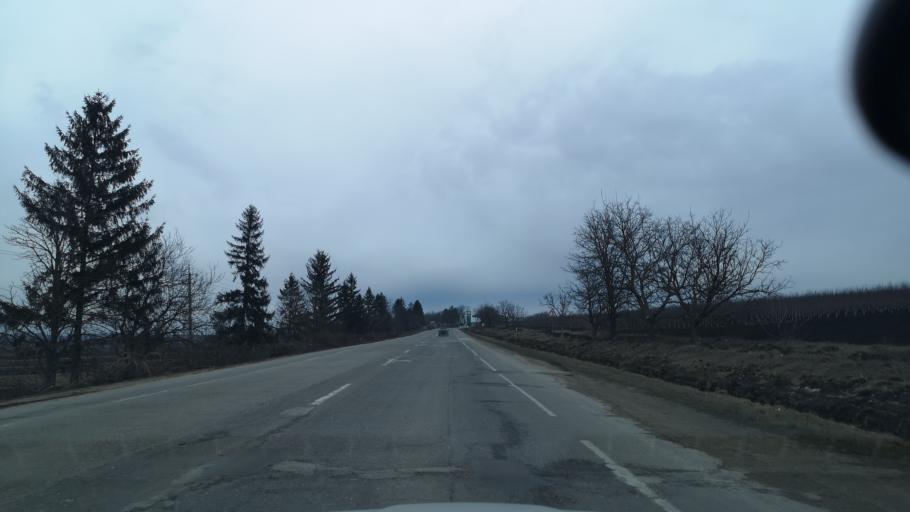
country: MD
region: Briceni
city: Briceni
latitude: 48.3354
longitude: 27.1178
